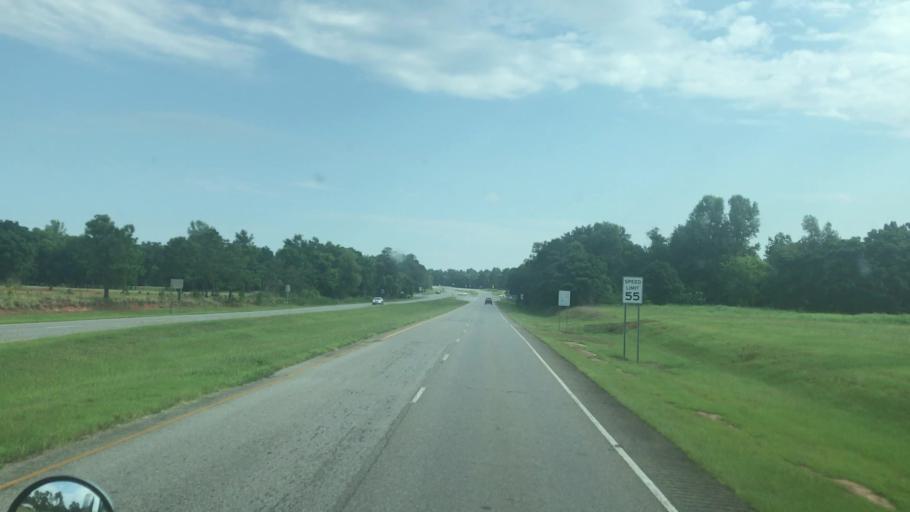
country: US
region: Georgia
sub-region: Early County
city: Blakely
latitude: 31.3767
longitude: -84.9215
